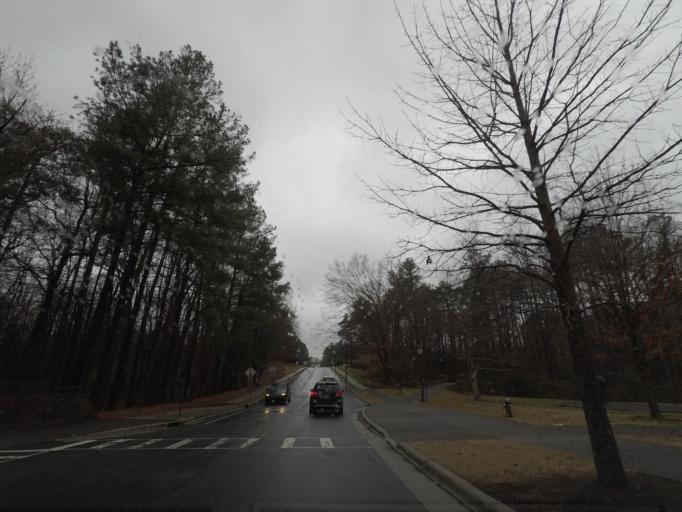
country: US
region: North Carolina
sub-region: Durham County
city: Durham
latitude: 36.0016
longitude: -78.9429
